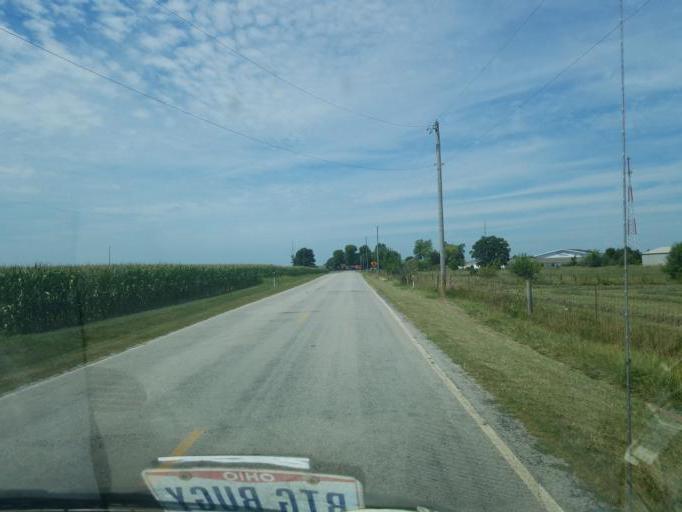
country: US
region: Ohio
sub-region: Madison County
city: West Jefferson
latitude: 40.0123
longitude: -83.3037
